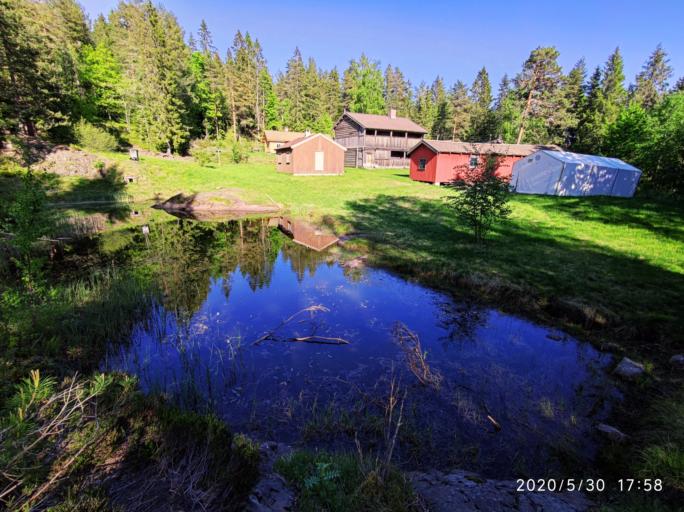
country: NO
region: Buskerud
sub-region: Drammen
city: Drammen
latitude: 59.7562
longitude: 10.2004
